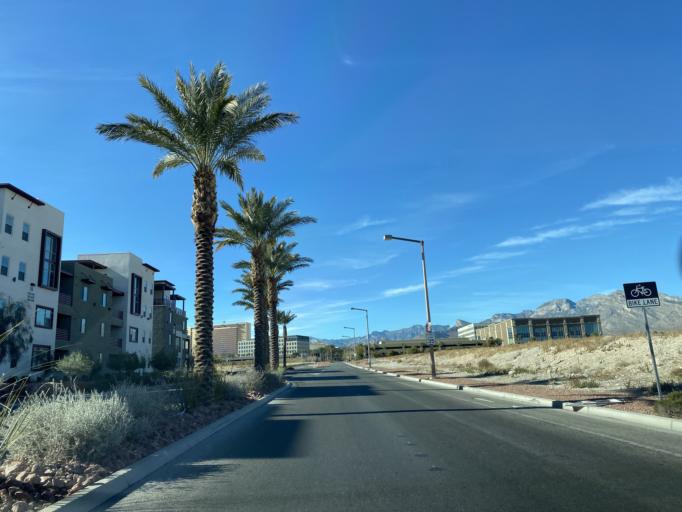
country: US
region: Nevada
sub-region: Clark County
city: Summerlin South
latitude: 36.1570
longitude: -115.3236
